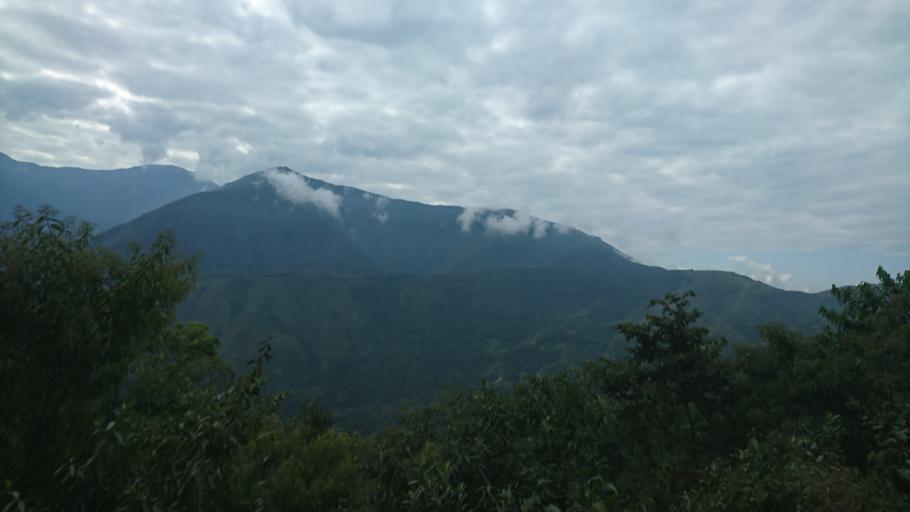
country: BO
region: La Paz
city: Coroico
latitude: -16.2276
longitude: -67.6789
